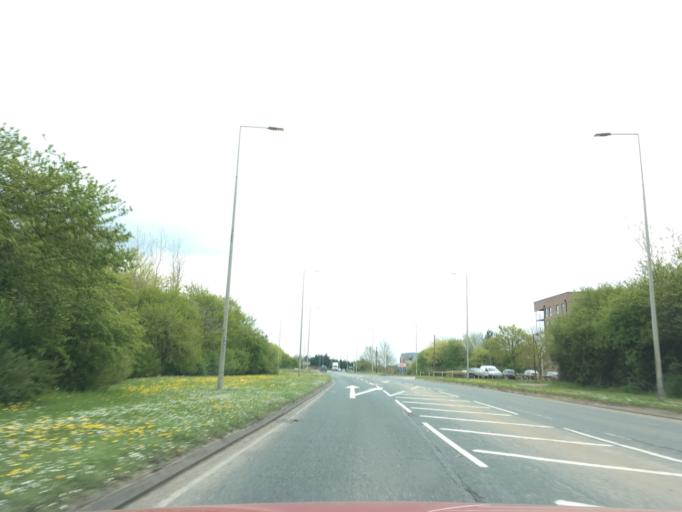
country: GB
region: England
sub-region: Milton Keynes
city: Broughton
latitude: 52.0437
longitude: -0.7196
